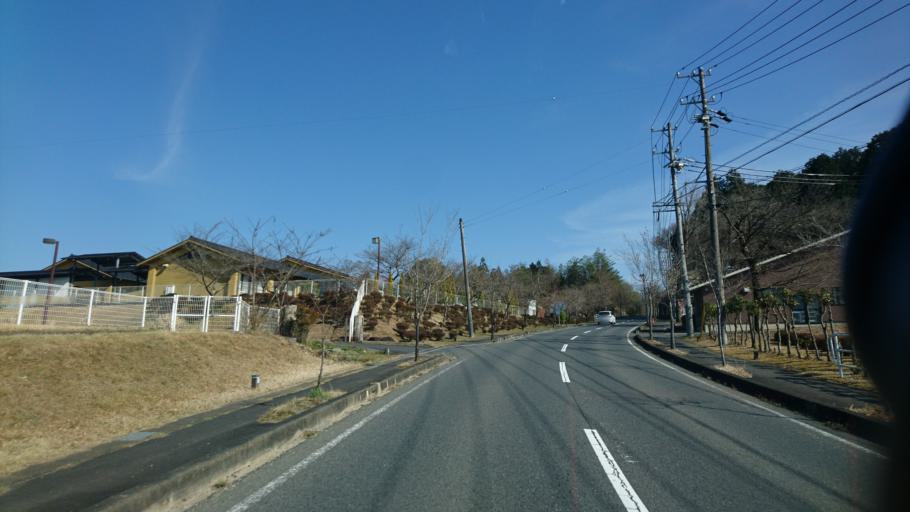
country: JP
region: Gifu
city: Nakatsugawa
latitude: 35.4645
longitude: 137.3912
